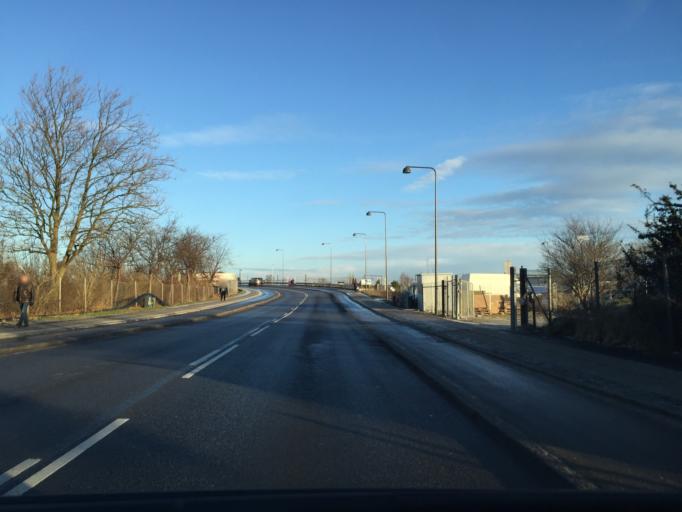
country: DK
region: Capital Region
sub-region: Hvidovre Kommune
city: Hvidovre
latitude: 55.6572
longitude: 12.5002
